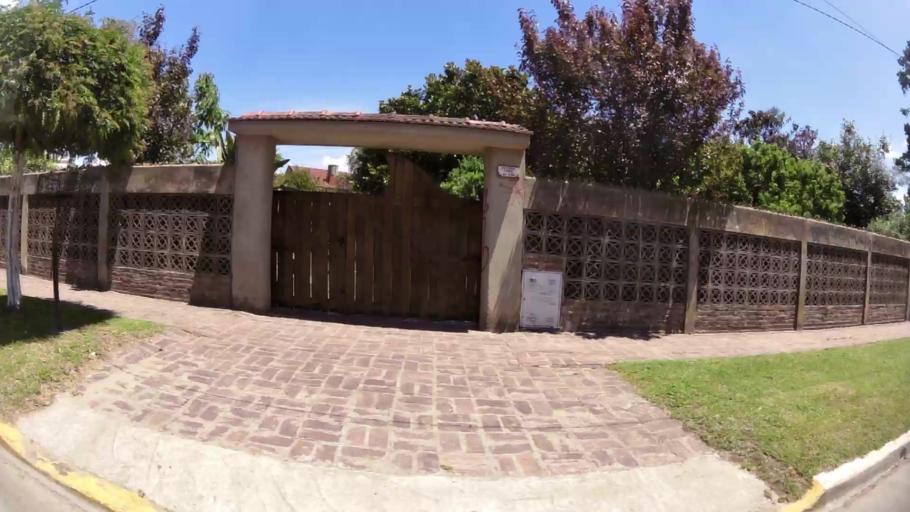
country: AR
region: Buenos Aires
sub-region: Partido de Merlo
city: Merlo
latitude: -34.6595
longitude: -58.7079
